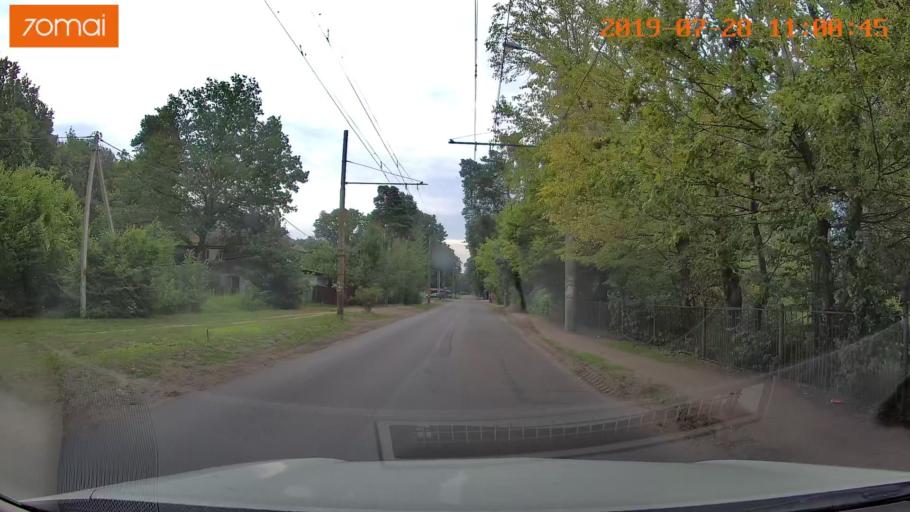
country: RU
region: Kaliningrad
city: Vzmorye
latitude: 54.7254
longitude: 20.3635
